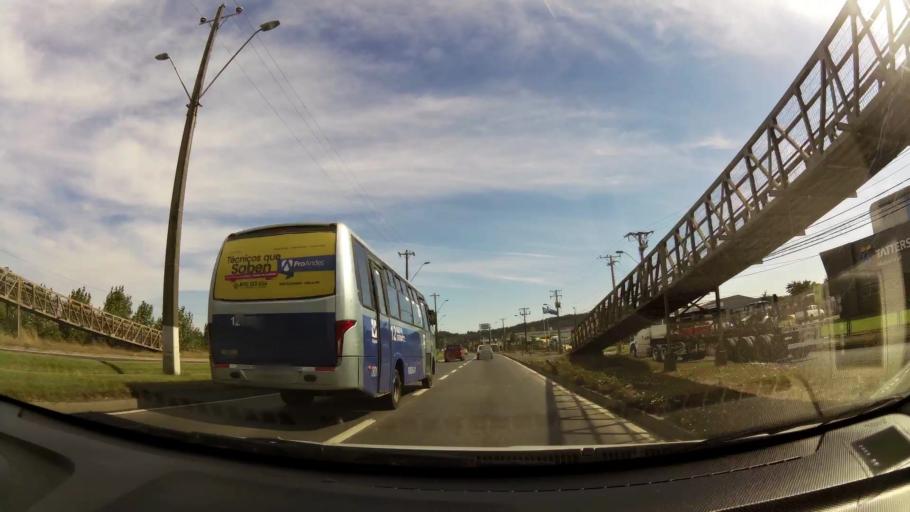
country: CL
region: Biobio
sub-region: Provincia de Concepcion
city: Talcahuano
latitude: -36.7682
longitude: -73.1155
